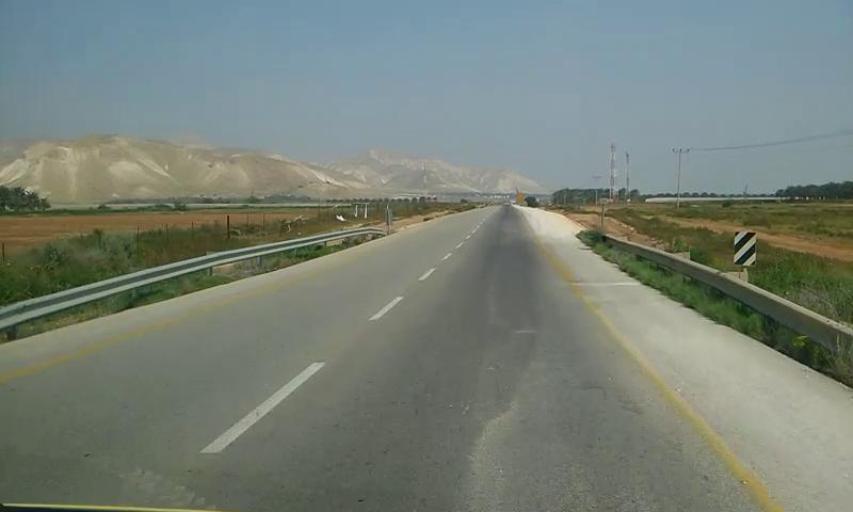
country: PS
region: West Bank
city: Al Fasayil
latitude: 32.0382
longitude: 35.4574
